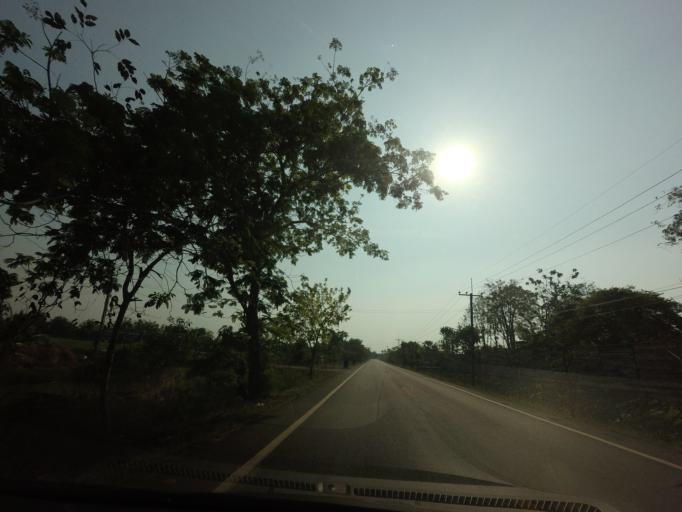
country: TH
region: Chachoengsao
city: Khlong Khuean
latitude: 13.8448
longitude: 101.1625
